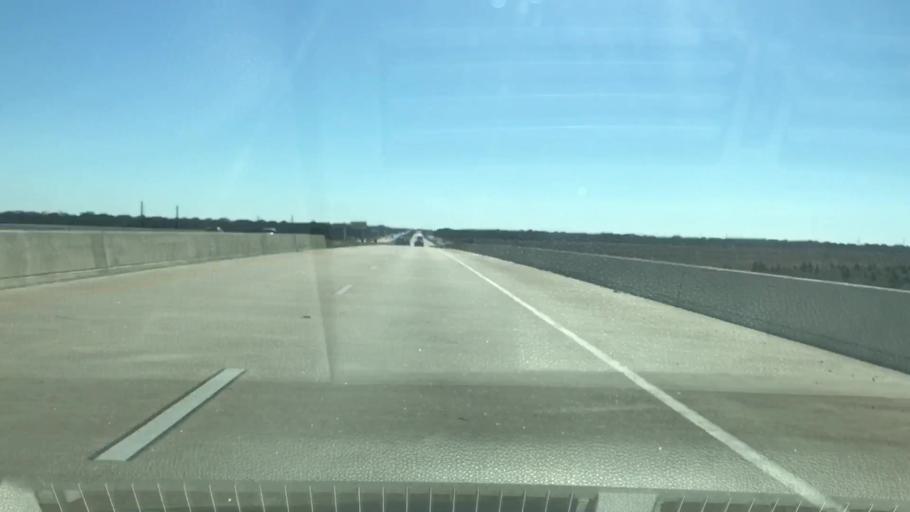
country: US
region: Texas
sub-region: Harris County
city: Cypress
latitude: 29.9778
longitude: -95.7697
